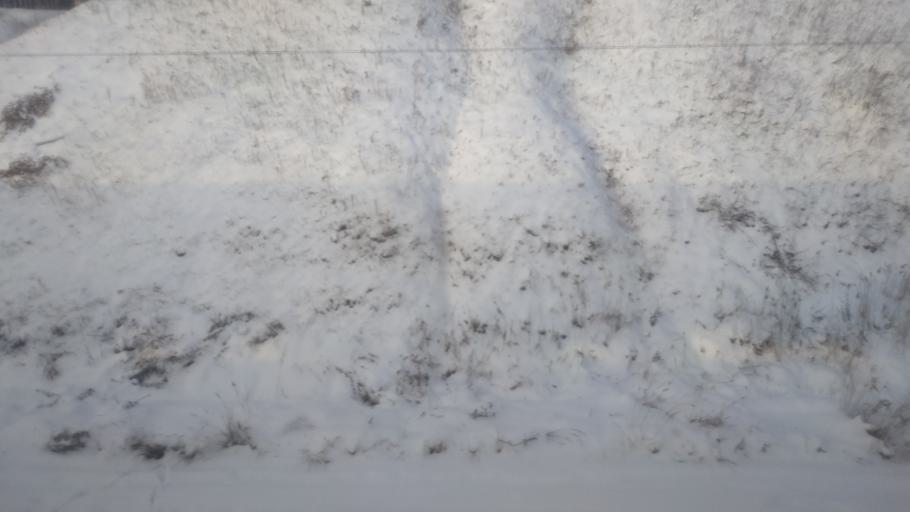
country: RU
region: Kirov
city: Sosnovka
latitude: 56.2530
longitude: 51.2324
